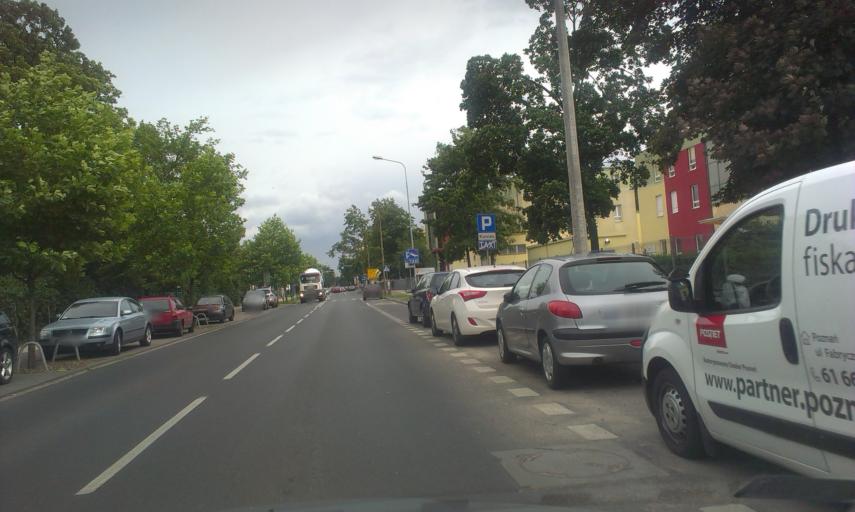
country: PL
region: Greater Poland Voivodeship
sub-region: Poznan
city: Poznan
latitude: 52.4130
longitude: 16.8870
